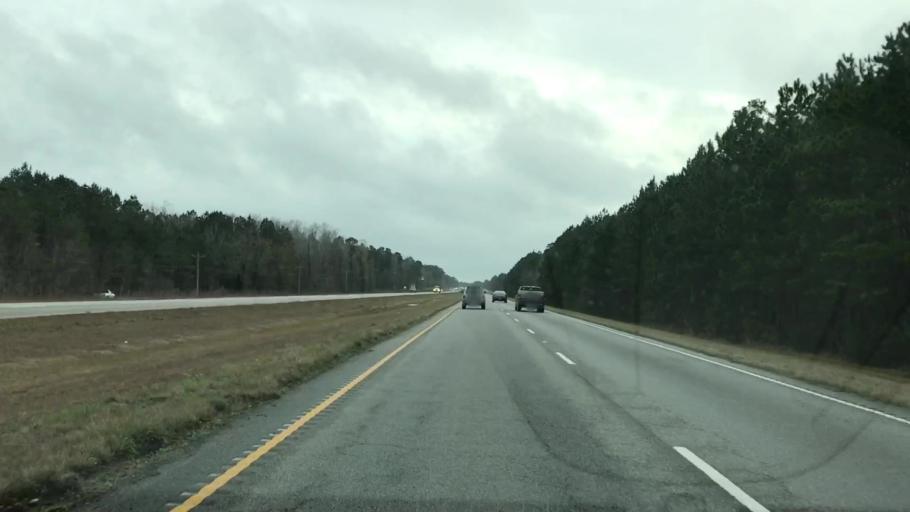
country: US
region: South Carolina
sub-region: Berkeley County
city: Goose Creek
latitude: 33.0814
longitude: -80.0327
